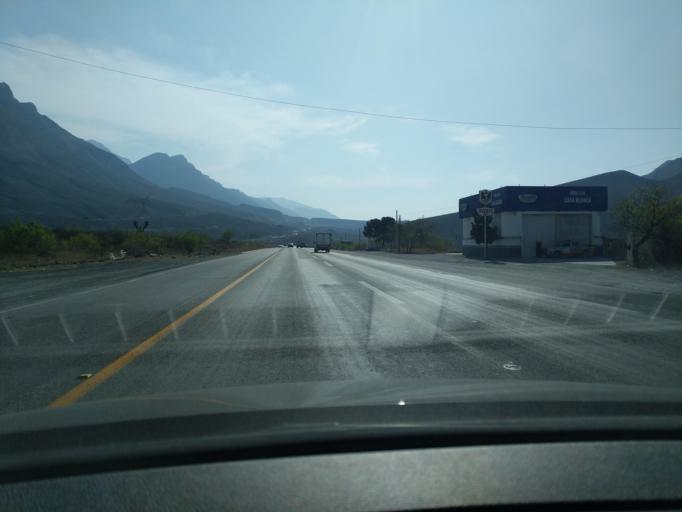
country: MX
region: Nuevo Leon
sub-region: Garcia
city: Las Torres de Guadalupe
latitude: 25.6596
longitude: -100.7160
